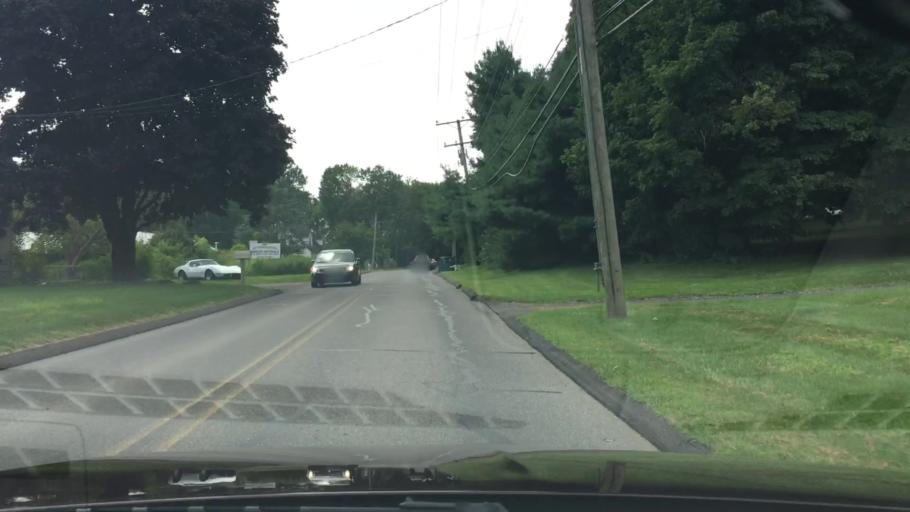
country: US
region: Connecticut
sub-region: New Haven County
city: Cheshire Village
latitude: 41.5406
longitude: -72.9030
